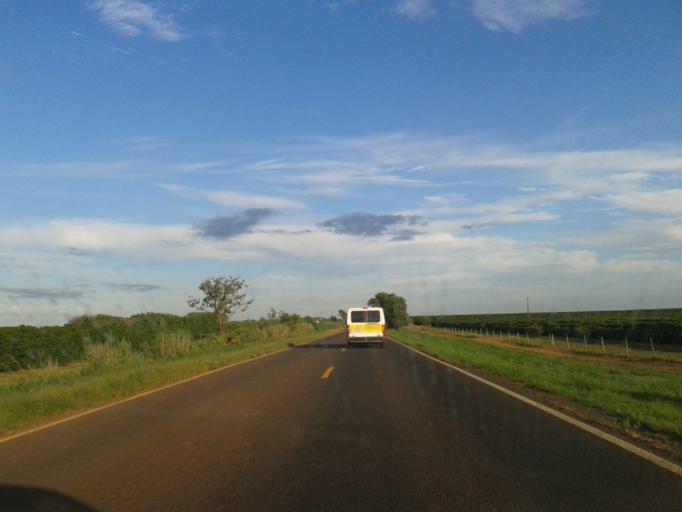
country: BR
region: Minas Gerais
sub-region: Araguari
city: Araguari
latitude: -18.6315
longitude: -48.2315
